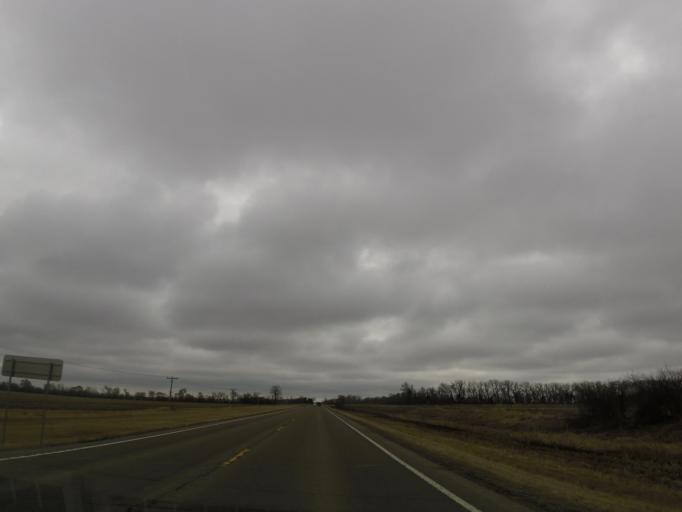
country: US
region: North Dakota
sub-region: Cass County
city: Casselton
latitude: 47.1496
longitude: -97.2176
